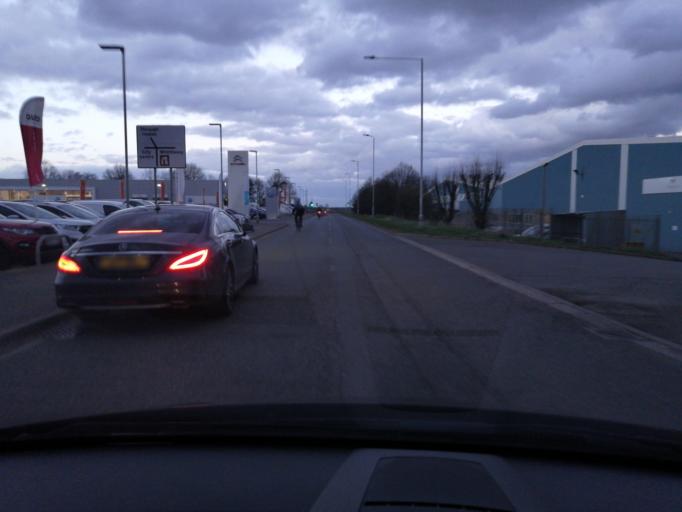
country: GB
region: England
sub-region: Peterborough
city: Eye
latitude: 52.5782
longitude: -0.2052
